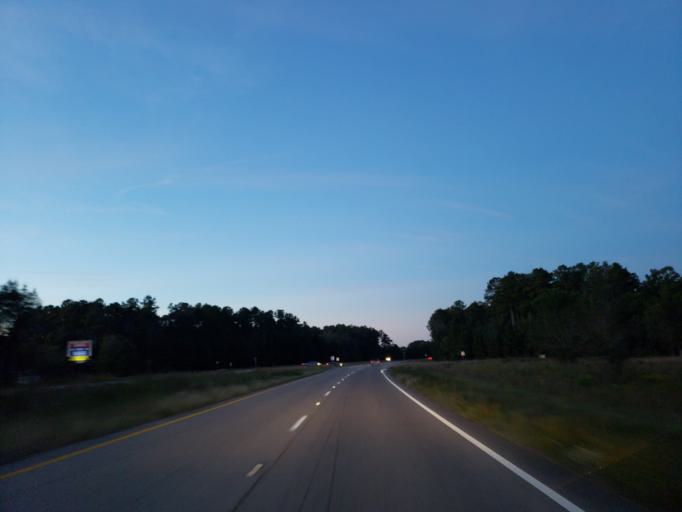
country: US
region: Mississippi
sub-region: Clarke County
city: Quitman
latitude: 31.8560
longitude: -88.7199
